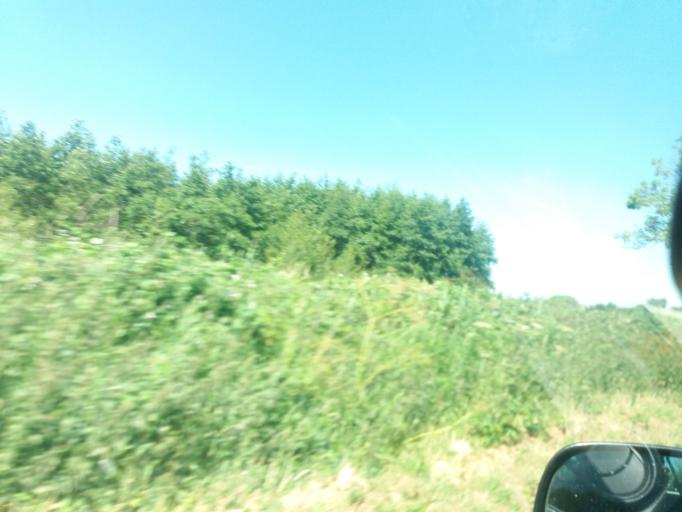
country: IE
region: Leinster
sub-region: Fingal County
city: Swords
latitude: 53.4824
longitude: -6.2708
